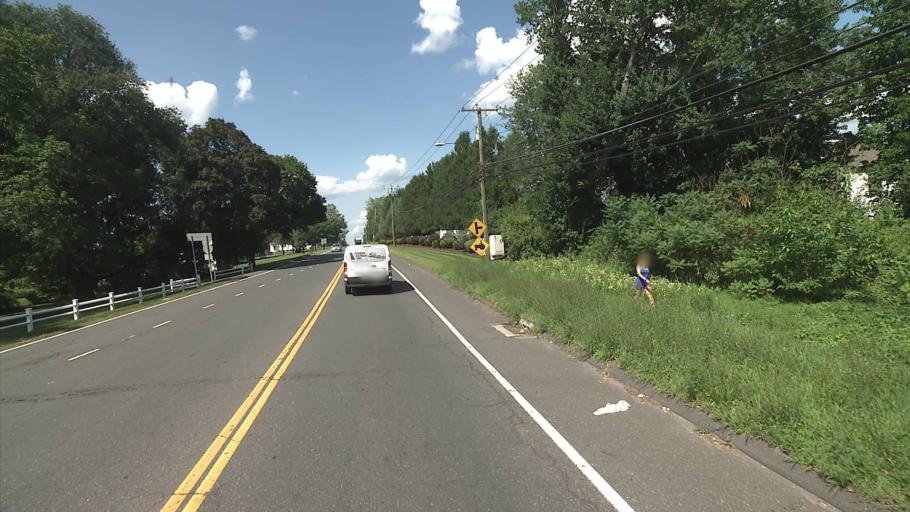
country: US
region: Connecticut
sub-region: Hartford County
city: Thompsonville
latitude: 41.9889
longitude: -72.6133
